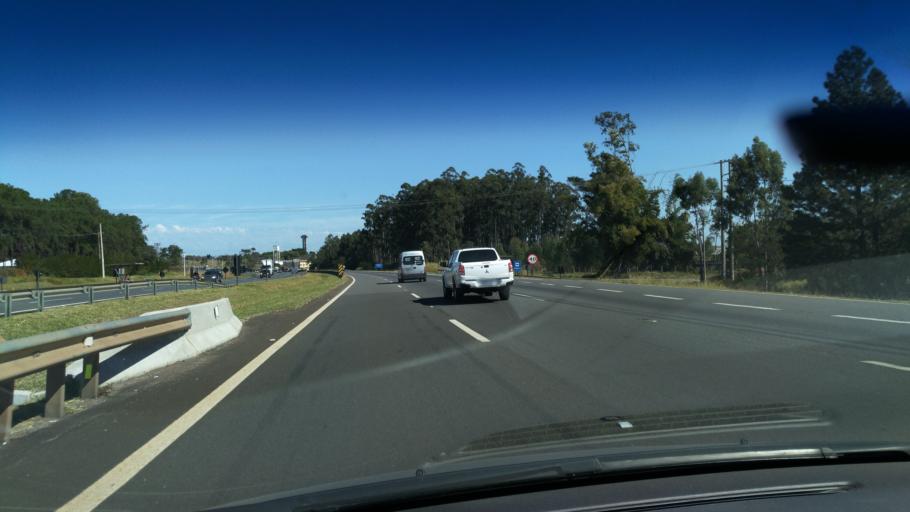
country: BR
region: Sao Paulo
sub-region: Jaguariuna
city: Jaguariuna
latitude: -22.7866
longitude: -47.0296
